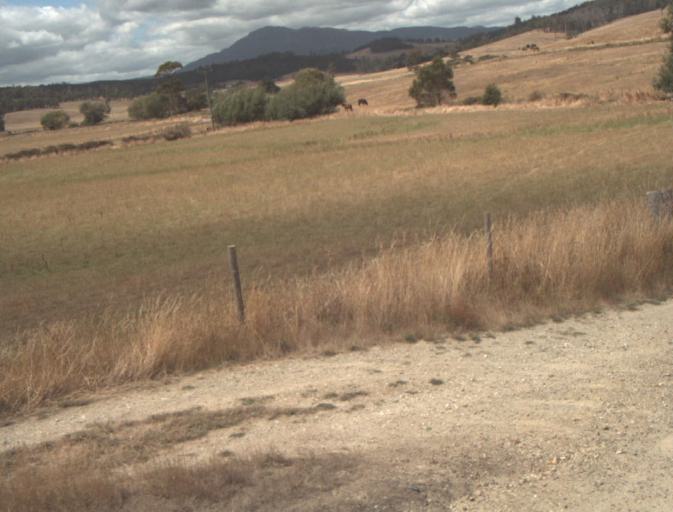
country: AU
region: Tasmania
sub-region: Launceston
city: Mayfield
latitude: -41.2112
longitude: 147.1427
